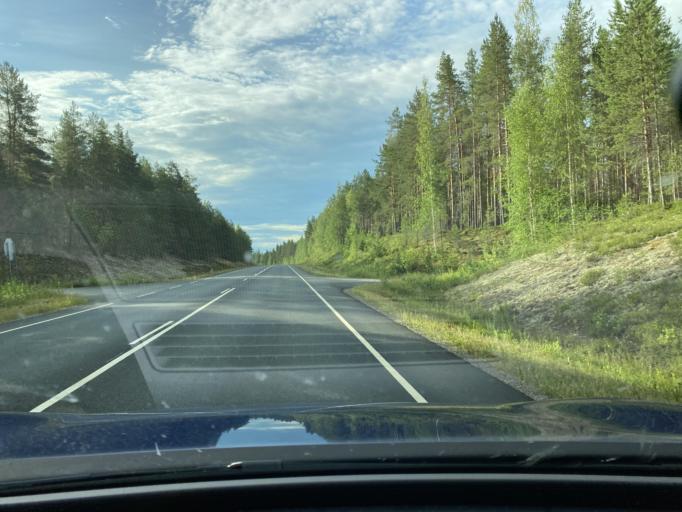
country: FI
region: Central Ostrobothnia
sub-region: Kaustinen
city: Veteli
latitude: 63.4146
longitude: 23.9492
